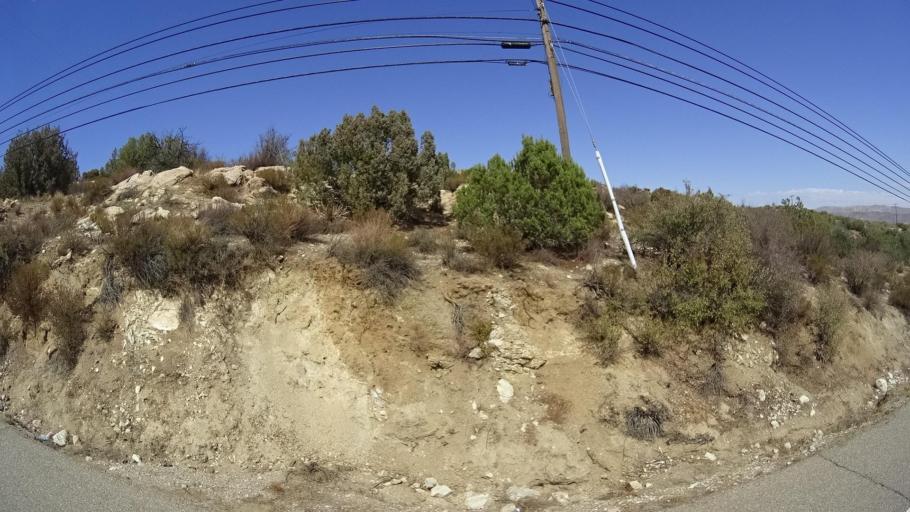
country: MX
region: Baja California
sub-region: Tecate
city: Cereso del Hongo
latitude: 32.6150
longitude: -116.2115
